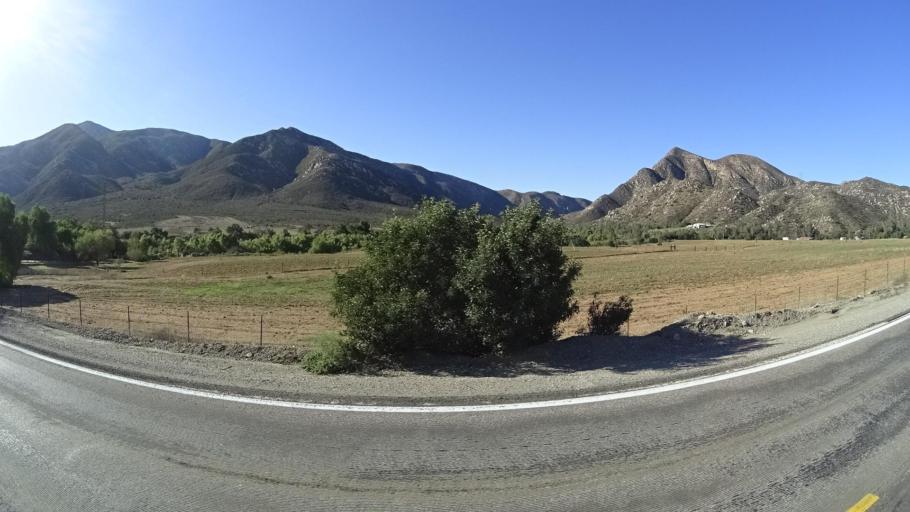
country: MX
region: Baja California
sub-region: Tecate
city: Lomas de Santa Anita
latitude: 32.6131
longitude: -116.7108
